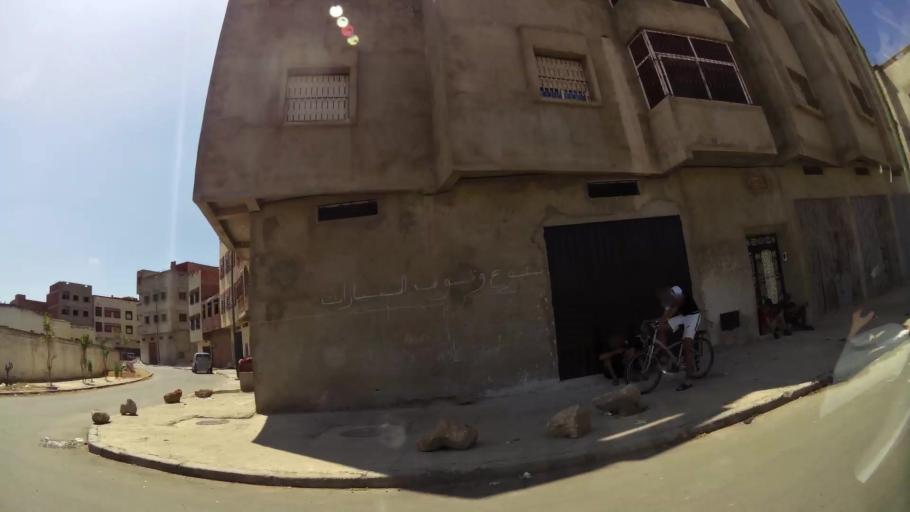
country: MA
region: Gharb-Chrarda-Beni Hssen
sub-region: Kenitra Province
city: Kenitra
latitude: 34.2423
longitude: -6.5396
